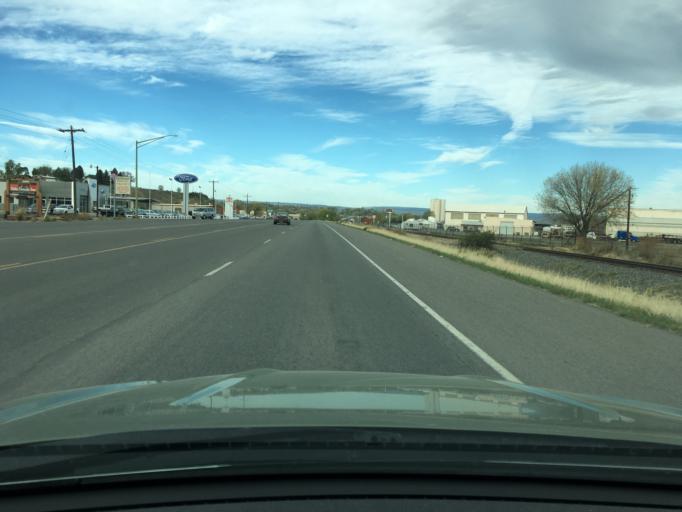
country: US
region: Colorado
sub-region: Delta County
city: Delta
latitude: 38.7501
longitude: -108.0607
